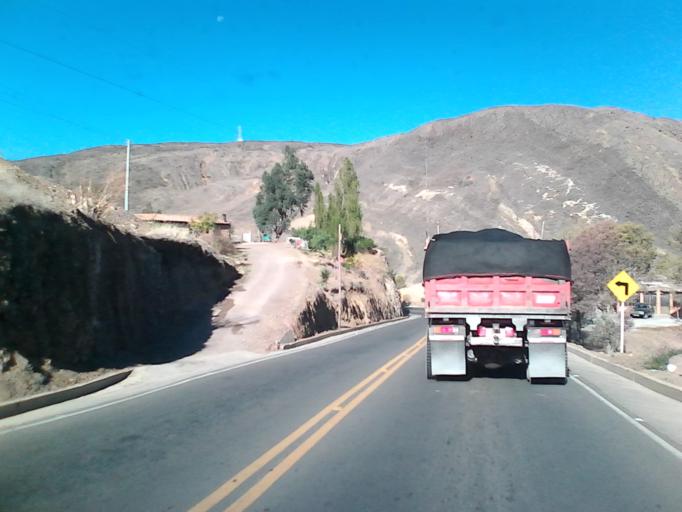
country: CO
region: Boyaca
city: Cucaita
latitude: 5.5566
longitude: -73.4974
